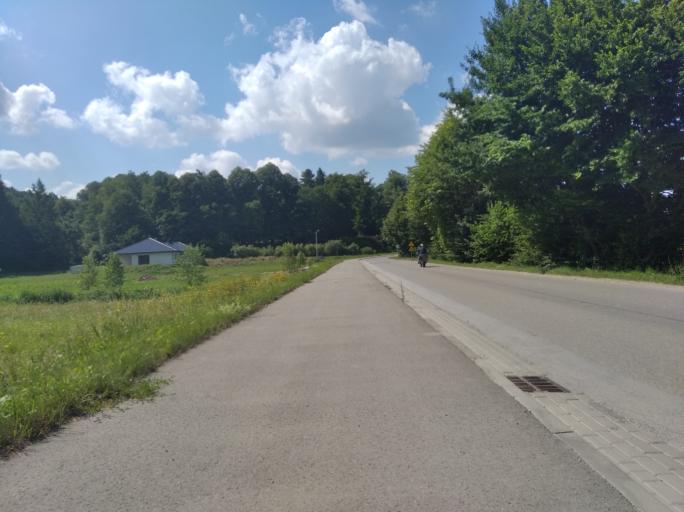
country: PL
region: Subcarpathian Voivodeship
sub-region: Powiat rzeszowski
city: Dynow
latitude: 49.7844
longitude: 22.2377
